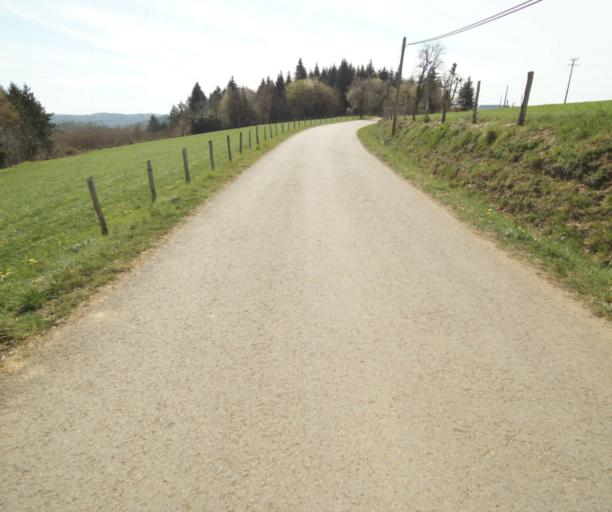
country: FR
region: Limousin
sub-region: Departement de la Correze
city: Naves
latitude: 45.3653
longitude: 1.8029
